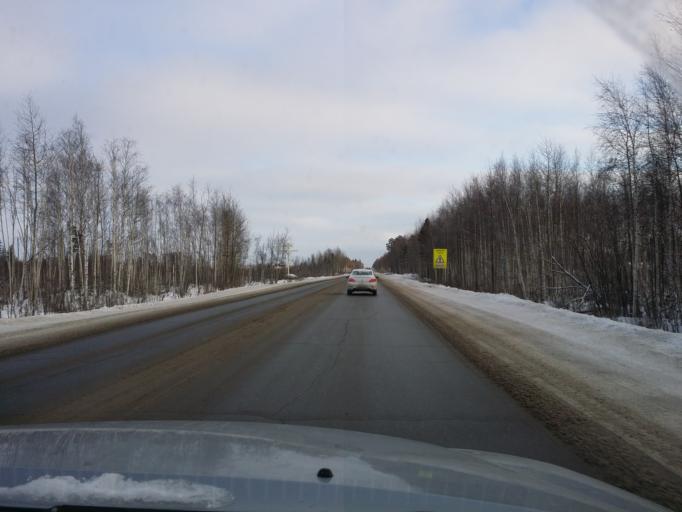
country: RU
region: Khanty-Mansiyskiy Avtonomnyy Okrug
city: Megion
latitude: 61.0634
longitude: 76.2713
